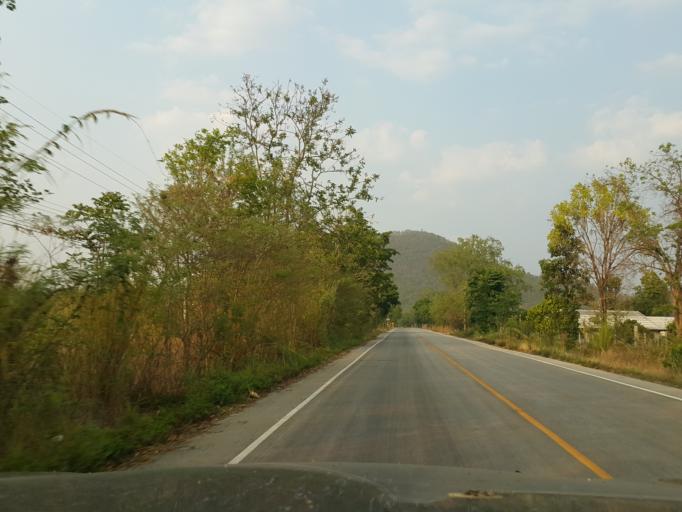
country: TH
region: Lamphun
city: Li
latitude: 17.8287
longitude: 98.9838
